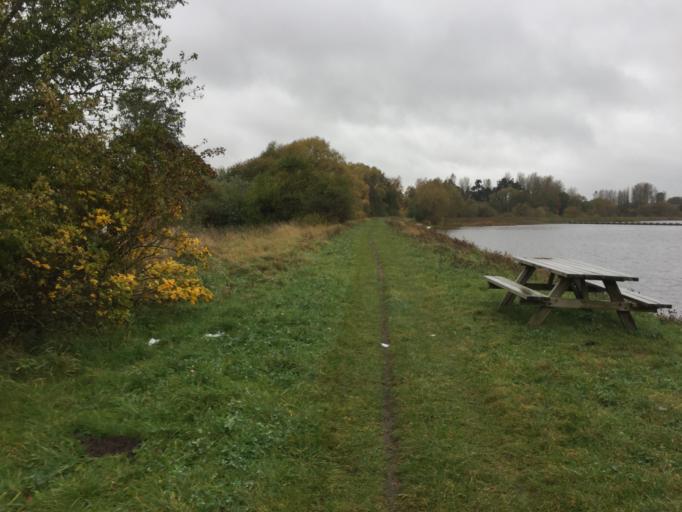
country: DK
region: Zealand
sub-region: Ringsted Kommune
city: Ringsted
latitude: 55.4816
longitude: 11.7531
